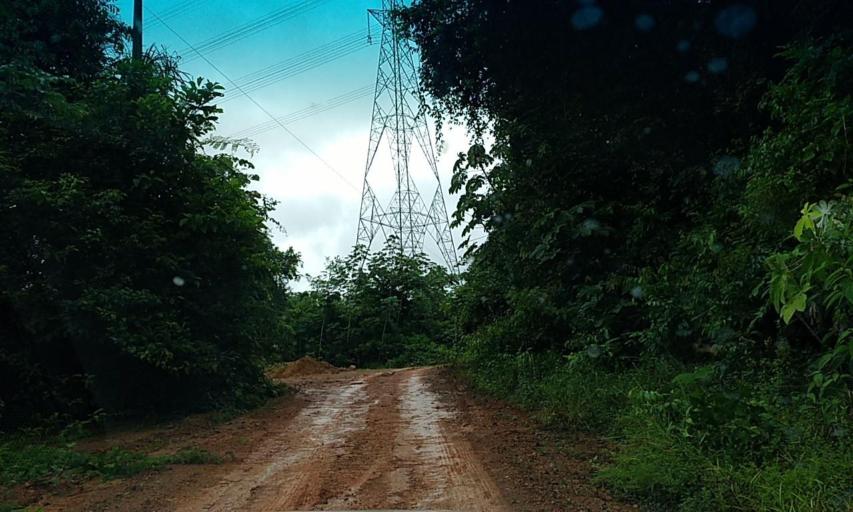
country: BR
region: Para
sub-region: Altamira
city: Altamira
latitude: -3.1143
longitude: -51.6032
